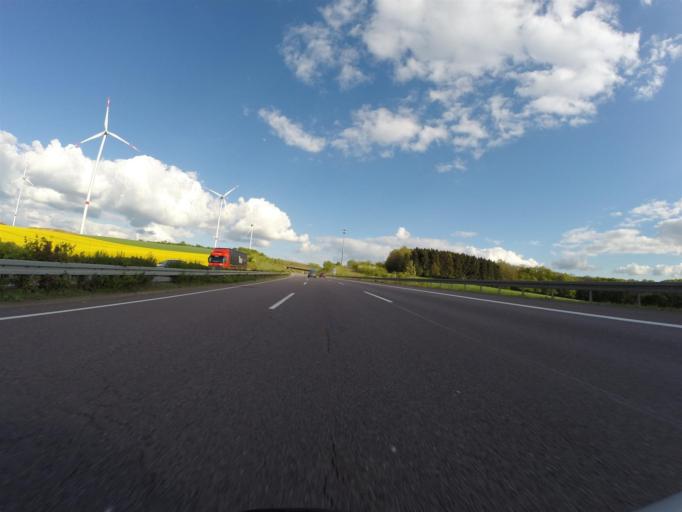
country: DE
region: Saarland
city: Perl
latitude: 49.4897
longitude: 6.4101
